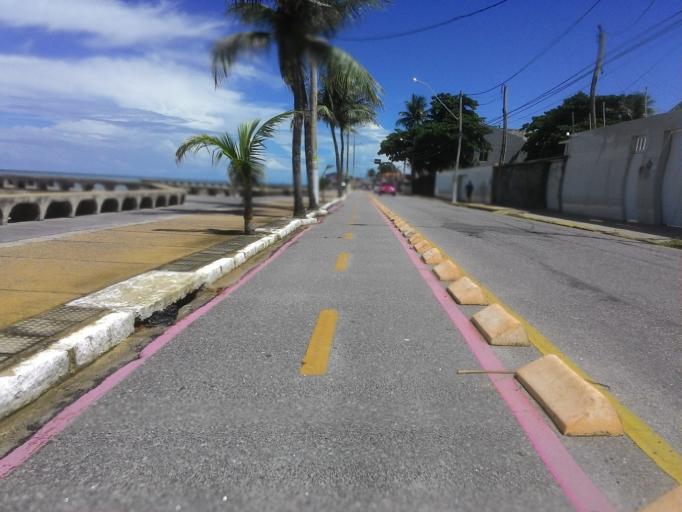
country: BR
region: Pernambuco
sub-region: Olinda
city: Olinda
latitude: -8.0091
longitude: -34.8415
